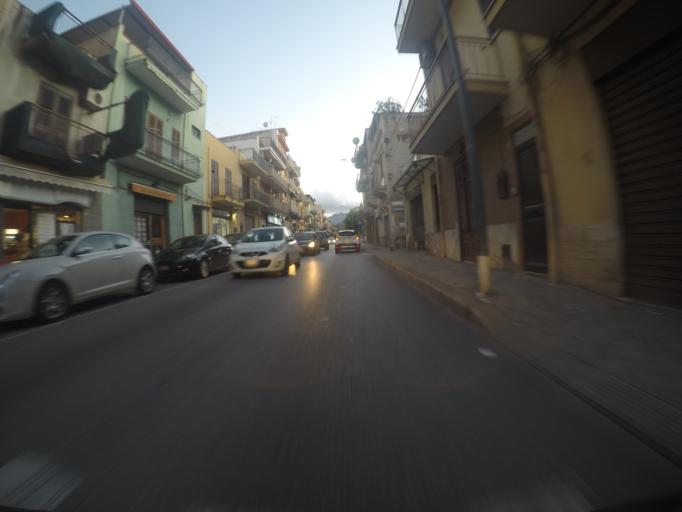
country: IT
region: Sicily
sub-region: Palermo
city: Capaci
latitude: 38.1757
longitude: 13.2421
